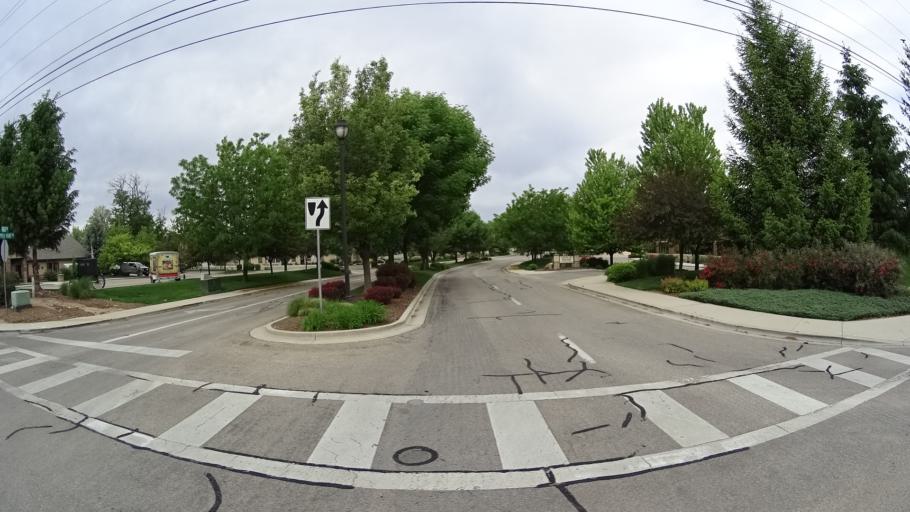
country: US
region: Idaho
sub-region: Ada County
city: Meridian
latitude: 43.5837
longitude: -116.3546
